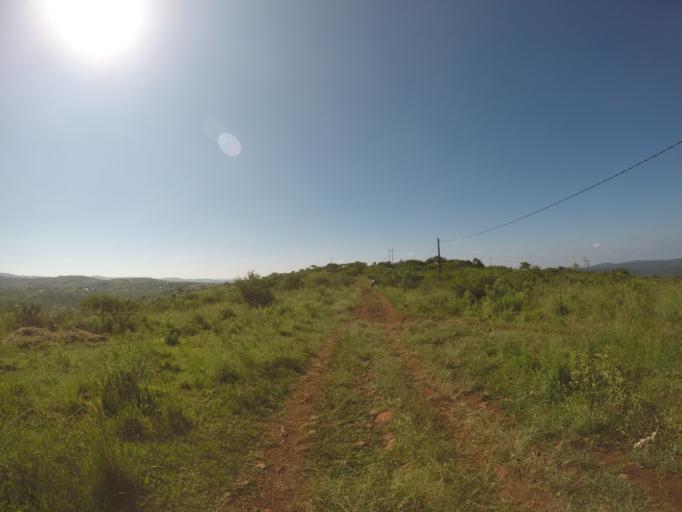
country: ZA
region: KwaZulu-Natal
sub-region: uThungulu District Municipality
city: Empangeni
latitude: -28.5723
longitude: 31.7105
